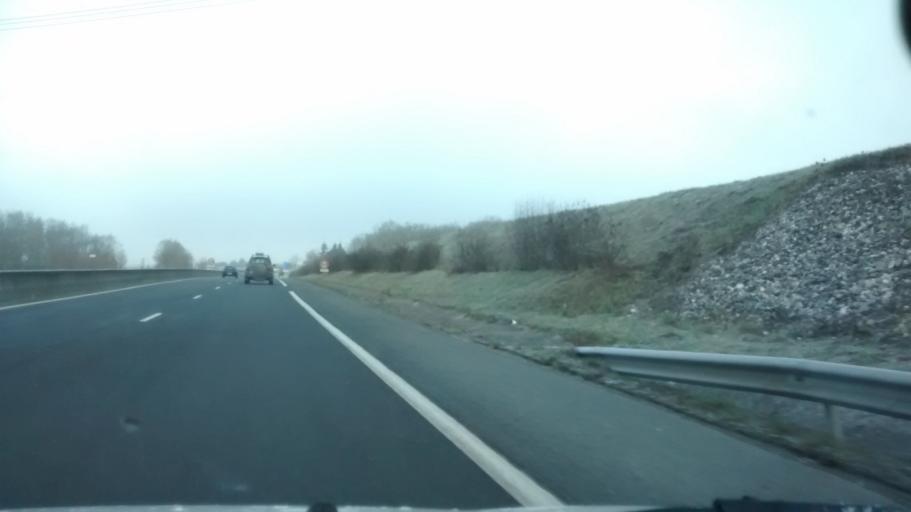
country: FR
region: Centre
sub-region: Departement d'Indre-et-Loire
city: Chambray-les-Tours
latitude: 47.3237
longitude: 0.6964
